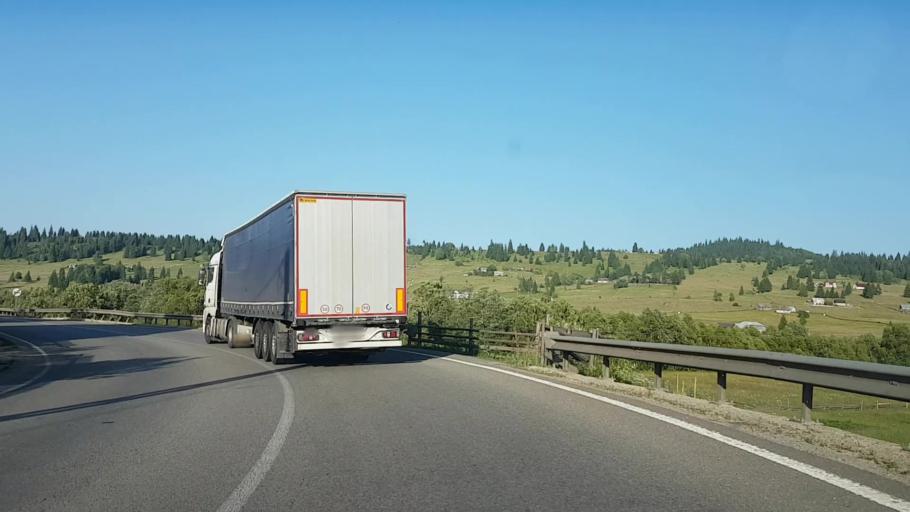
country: RO
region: Suceava
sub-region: Comuna Cosna
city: Cosna
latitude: 47.3382
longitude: 25.1705
